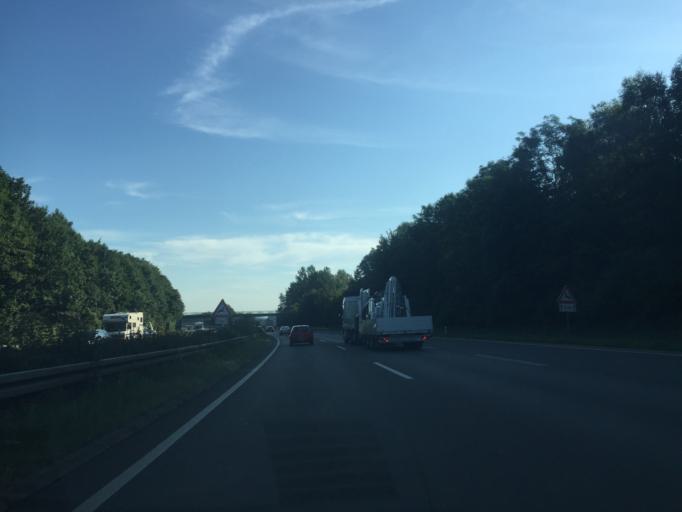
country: DE
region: North Rhine-Westphalia
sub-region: Regierungsbezirk Arnsberg
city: Luedenscheid
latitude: 51.1956
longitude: 7.6723
